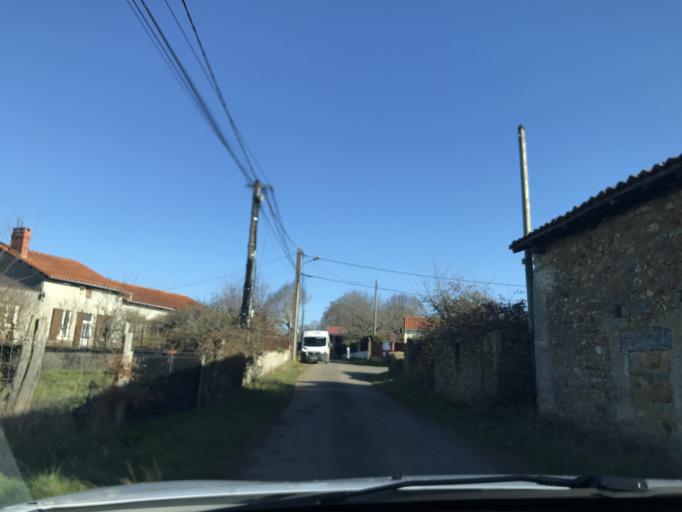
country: FR
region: Poitou-Charentes
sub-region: Departement de la Charente
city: Chasseneuil-sur-Bonnieure
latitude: 45.8452
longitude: 0.5152
